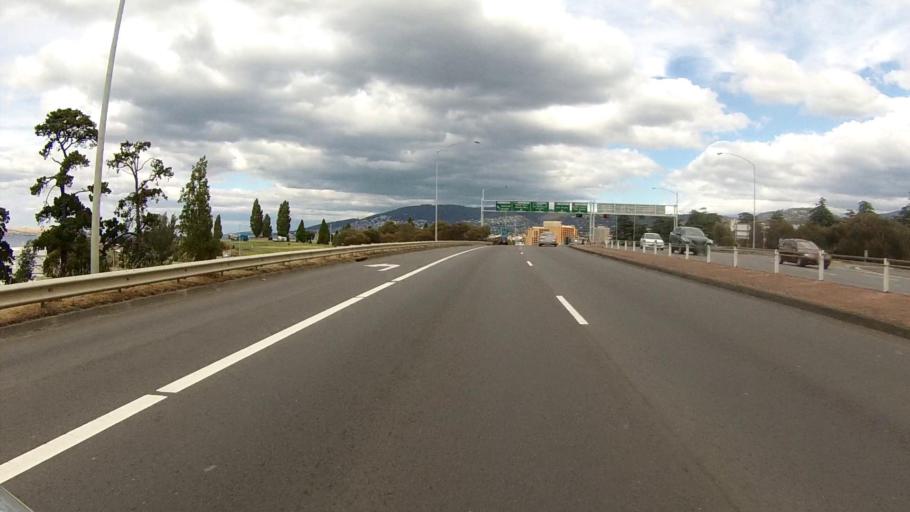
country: AU
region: Tasmania
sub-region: Hobart
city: Hobart
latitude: -42.8742
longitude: 147.3343
